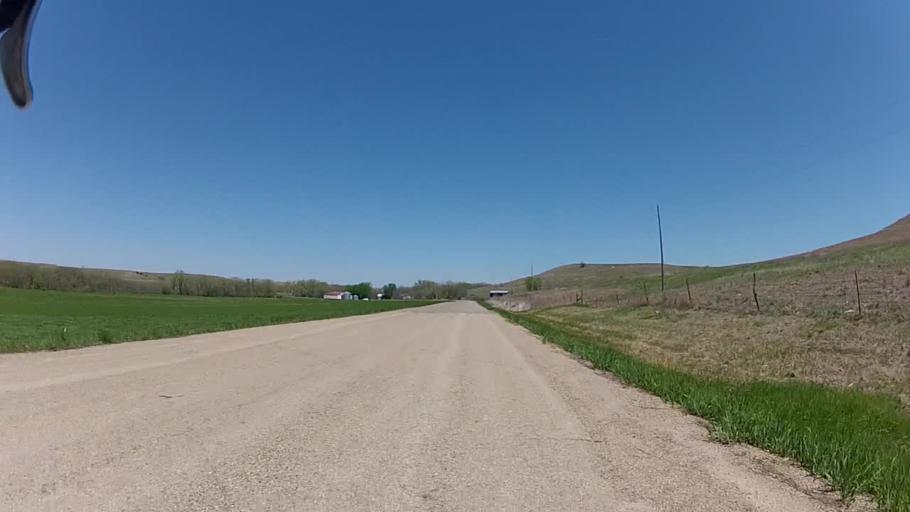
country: US
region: Kansas
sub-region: Riley County
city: Ogden
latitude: 38.9844
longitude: -96.5905
